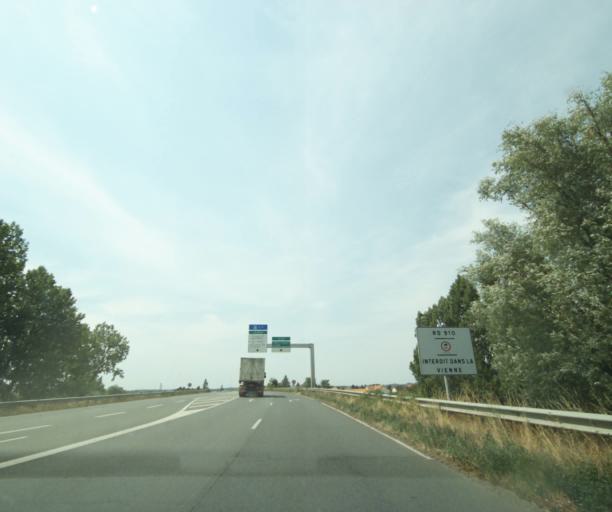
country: FR
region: Poitou-Charentes
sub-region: Departement de la Vienne
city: Antran
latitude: 46.8372
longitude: 0.5518
